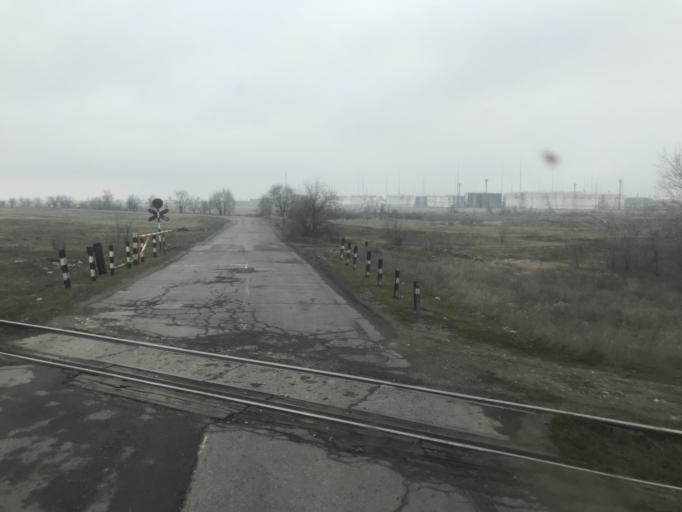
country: RU
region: Volgograd
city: Svetlyy Yar
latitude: 48.4945
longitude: 44.6524
